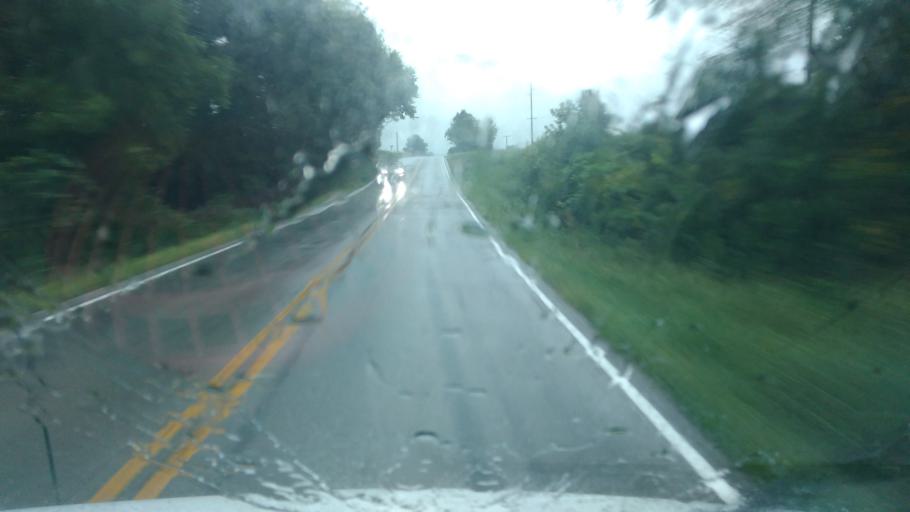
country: US
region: Ohio
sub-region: Scioto County
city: West Portsmouth
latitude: 38.6432
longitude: -83.1150
